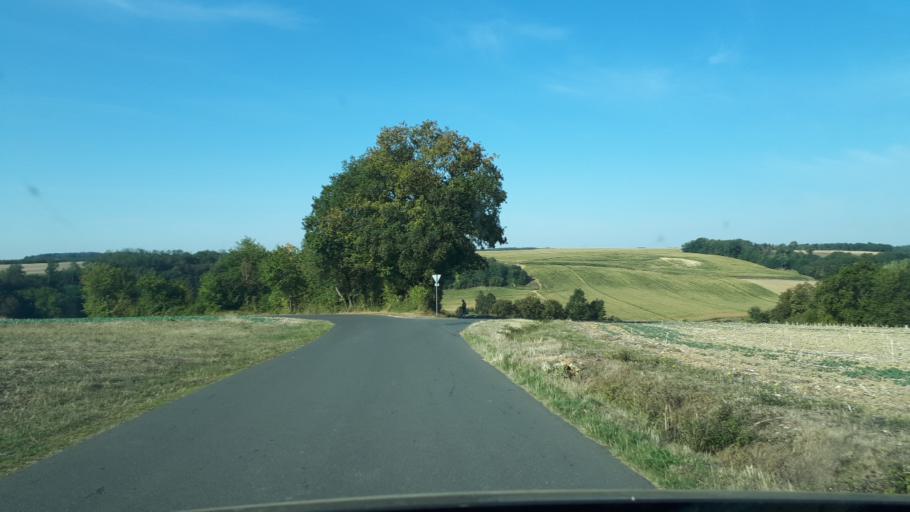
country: FR
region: Centre
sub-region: Departement du Loir-et-Cher
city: Lunay
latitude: 47.8302
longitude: 0.9451
